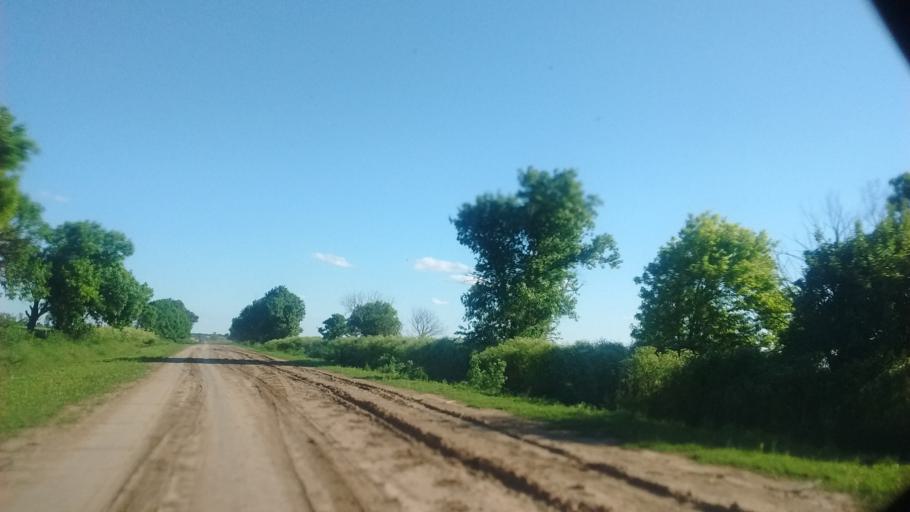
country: AR
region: Santa Fe
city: Funes
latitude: -32.8759
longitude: -60.7984
